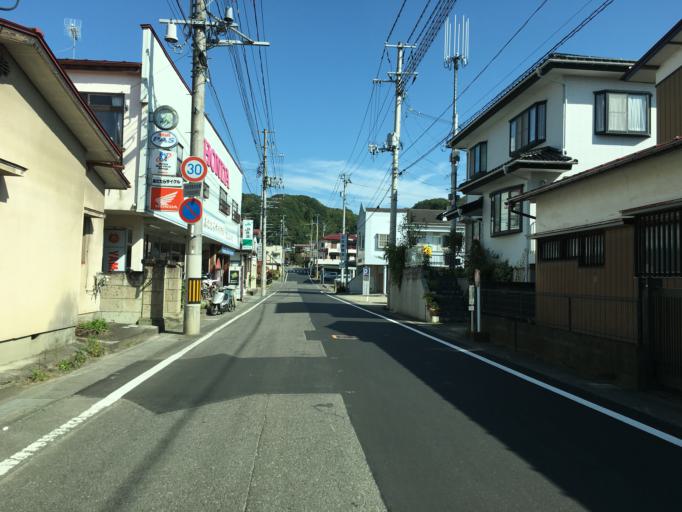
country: JP
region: Fukushima
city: Nihommatsu
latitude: 37.5899
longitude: 140.4273
